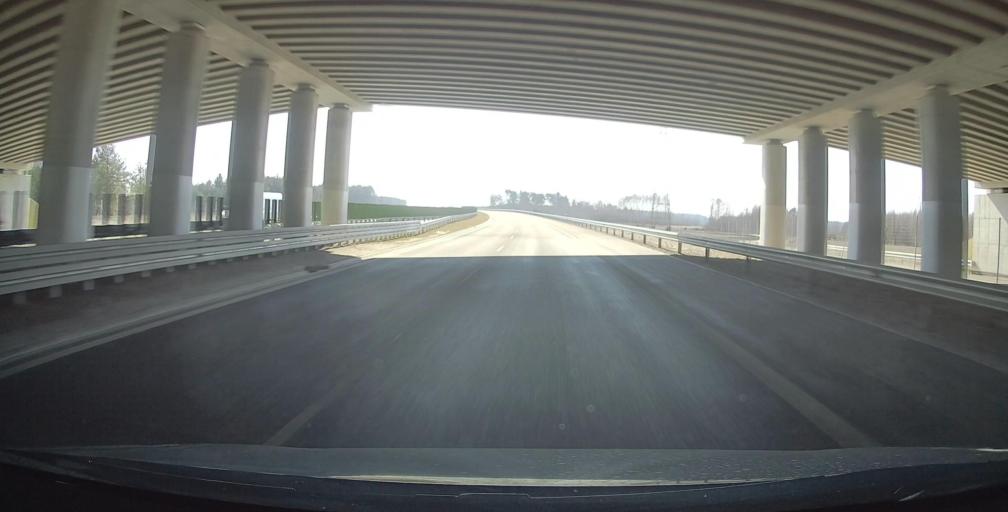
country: PL
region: Subcarpathian Voivodeship
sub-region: Powiat nizanski
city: Konczyce
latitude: 50.4215
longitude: 22.1283
